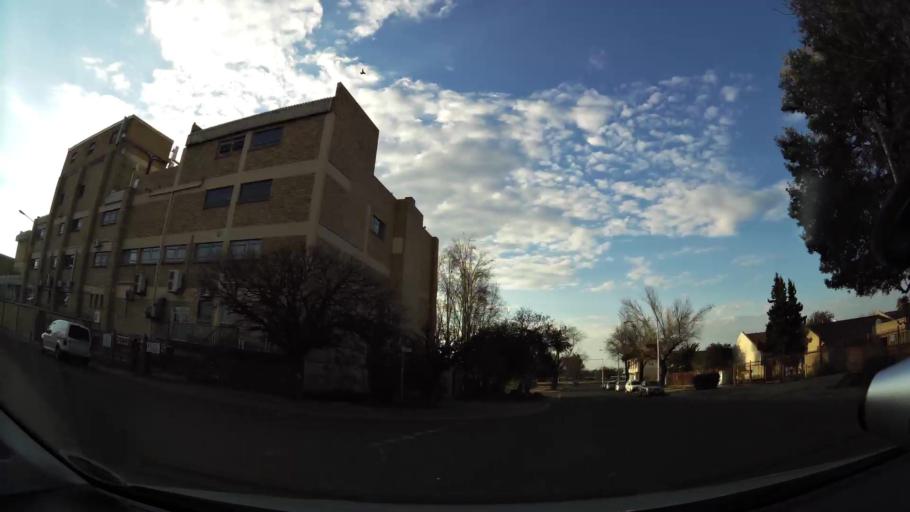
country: ZA
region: Orange Free State
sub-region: Mangaung Metropolitan Municipality
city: Bloemfontein
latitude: -29.1350
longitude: 26.1952
